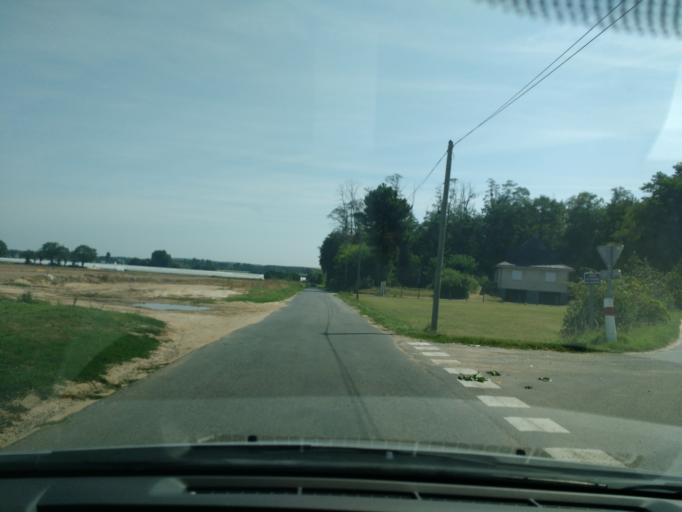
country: FR
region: Pays de la Loire
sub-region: Departement de Maine-et-Loire
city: Maze
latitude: 47.4733
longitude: -0.2689
